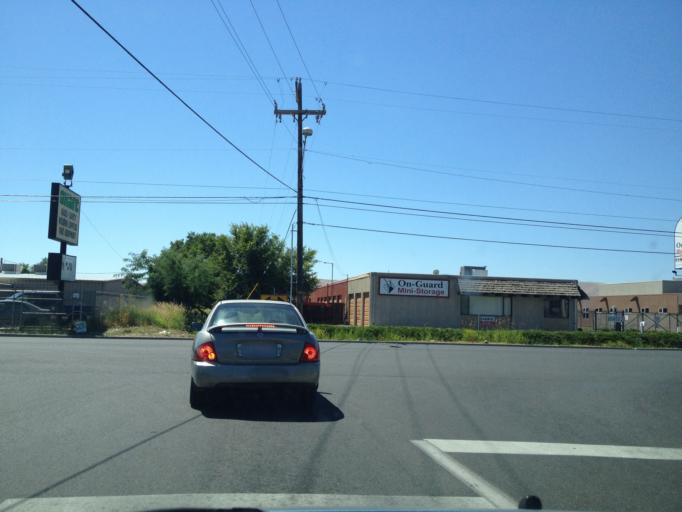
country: US
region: Washington
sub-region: Yakima County
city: Union Gap
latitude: 46.5780
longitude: -120.4882
